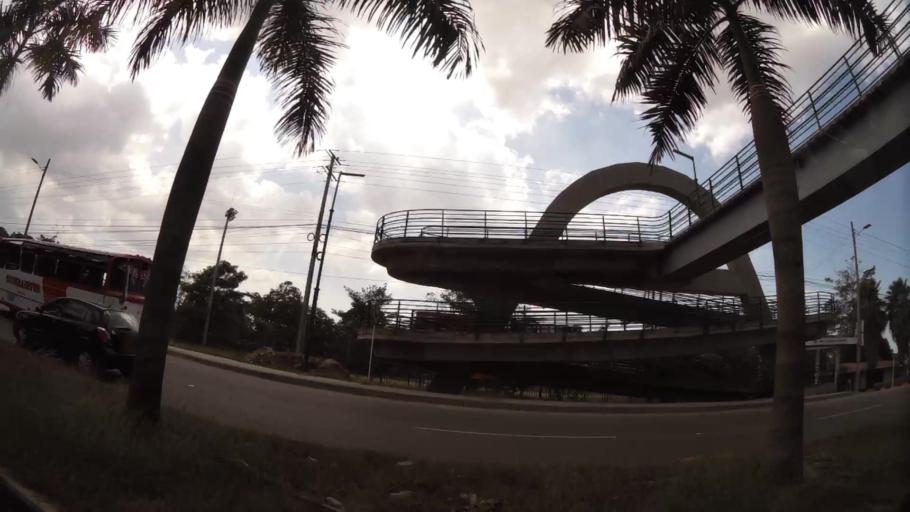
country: CO
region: Bolivar
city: Cartagena
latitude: 10.3751
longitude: -75.4590
